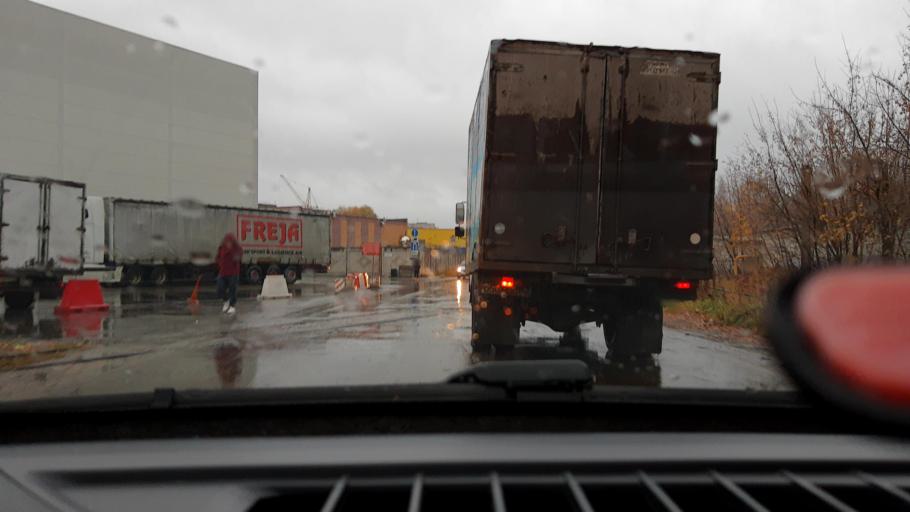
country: RU
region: Nizjnij Novgorod
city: Gorbatovka
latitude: 56.3160
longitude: 43.8594
